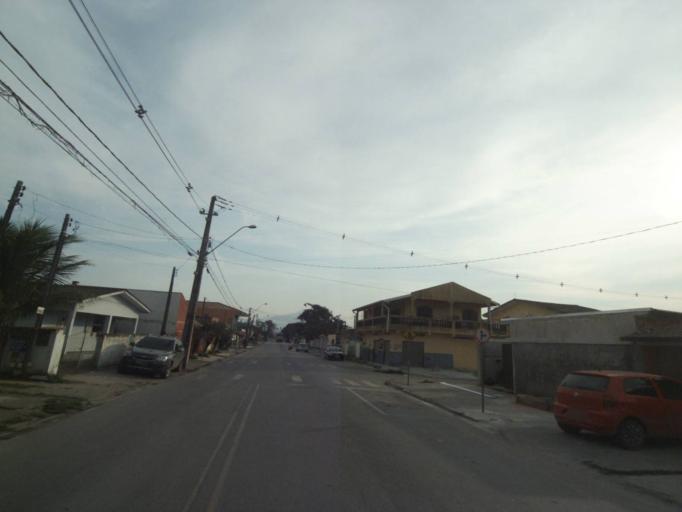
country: BR
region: Parana
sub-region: Paranagua
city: Paranagua
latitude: -25.5192
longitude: -48.5334
